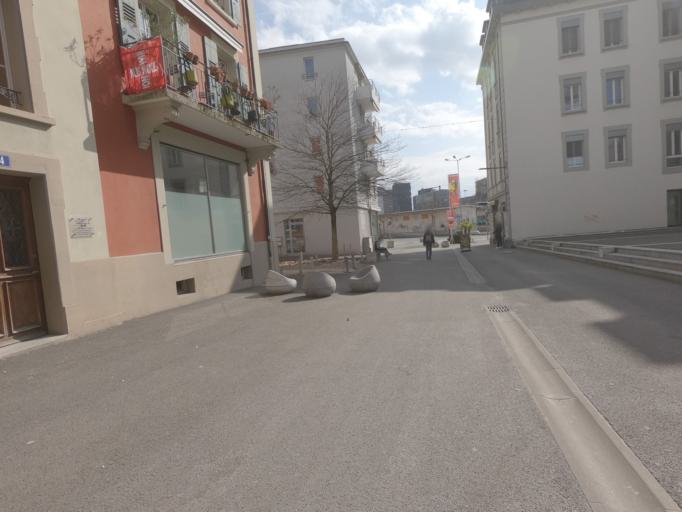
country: CH
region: Vaud
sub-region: Ouest Lausannois District
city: Renens
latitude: 46.5373
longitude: 6.5822
